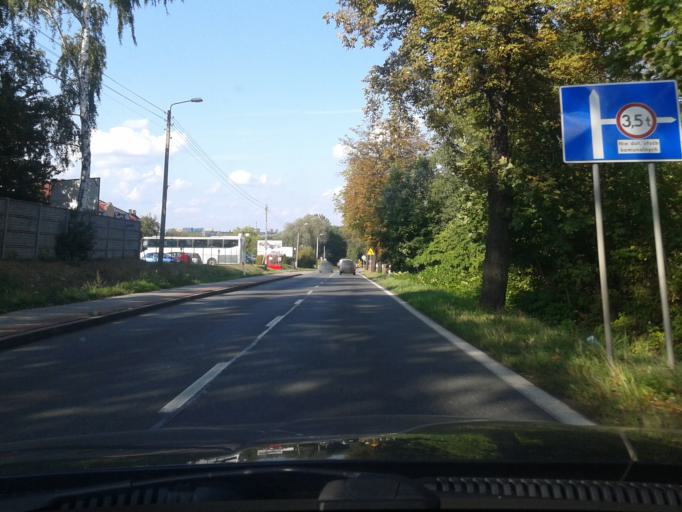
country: PL
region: Silesian Voivodeship
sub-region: Powiat wodzislawski
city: Turza Slaska
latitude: 49.9839
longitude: 18.4533
